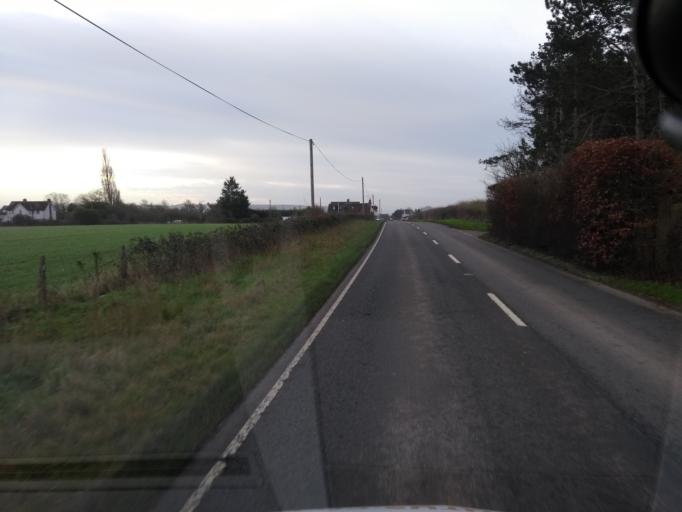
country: GB
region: England
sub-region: Somerset
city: Westonzoyland
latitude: 51.1165
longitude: -2.8523
